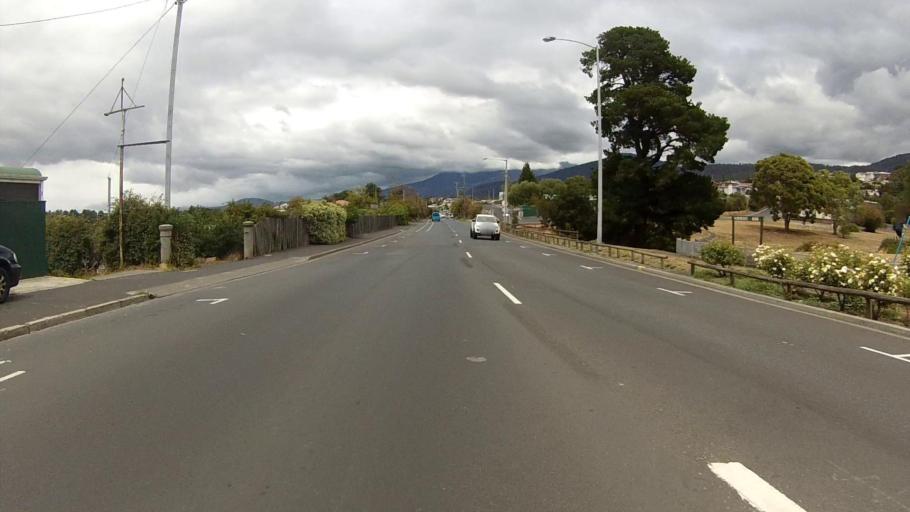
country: AU
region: Tasmania
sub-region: Glenorchy
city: Claremont
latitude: -42.7817
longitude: 147.2524
